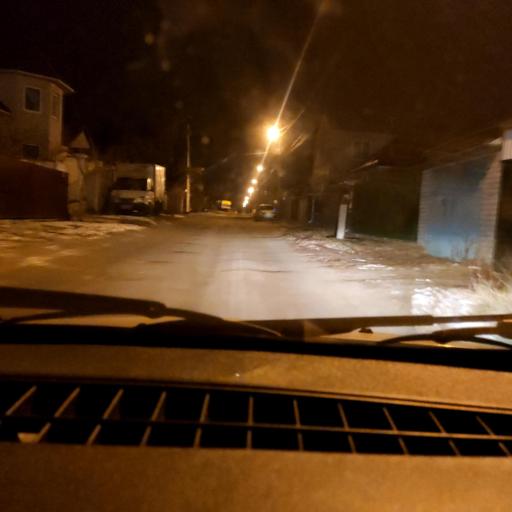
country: RU
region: Voronezj
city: Somovo
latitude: 51.7400
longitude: 39.2654
